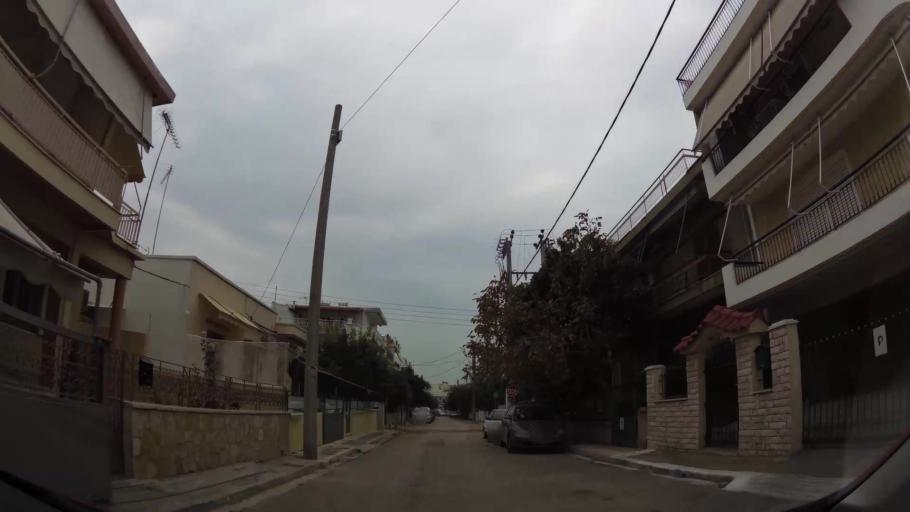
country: GR
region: Attica
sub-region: Nomarchia Athinas
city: Agioi Anargyroi
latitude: 38.0352
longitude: 23.7129
